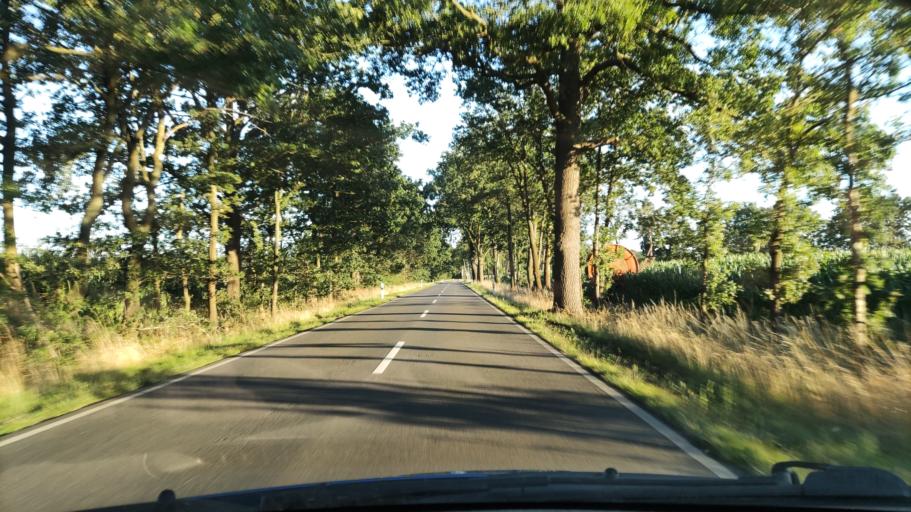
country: DE
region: Lower Saxony
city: Jameln
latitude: 53.0364
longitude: 11.1287
